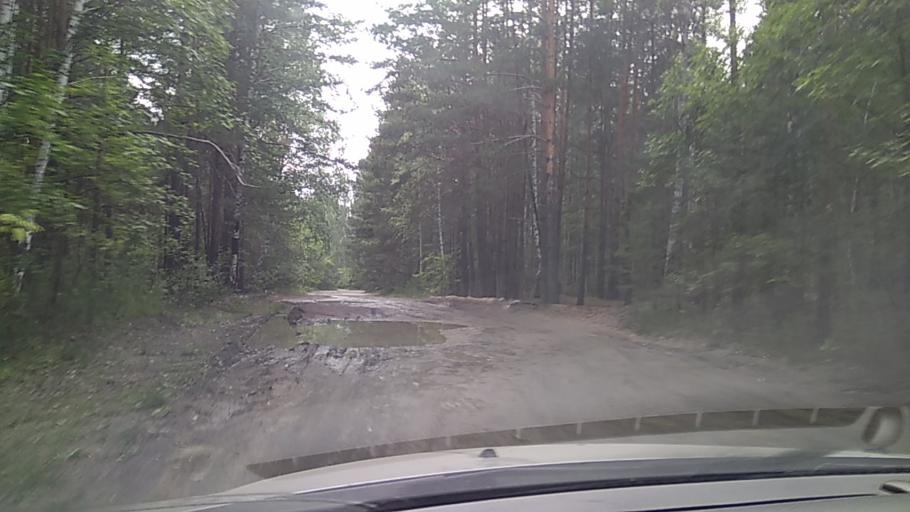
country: RU
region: Chelyabinsk
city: Kyshtym
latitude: 55.6782
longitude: 60.5844
